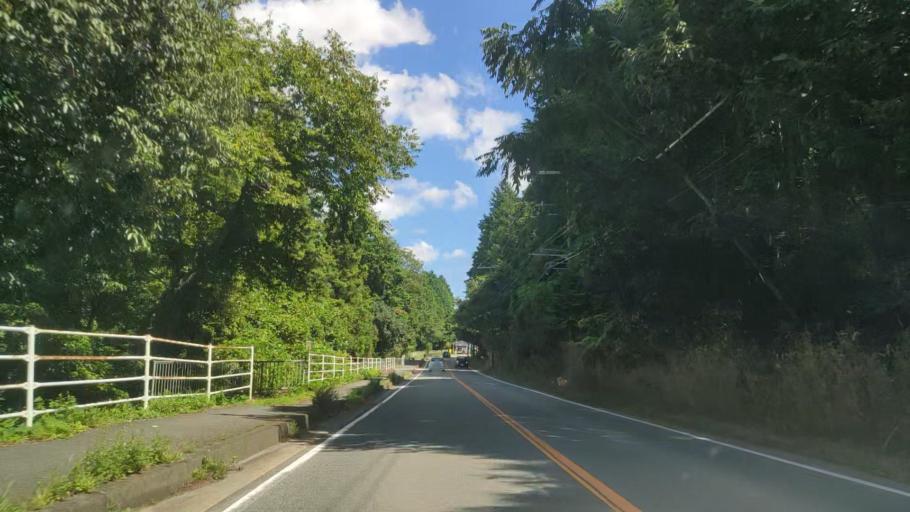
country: JP
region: Hyogo
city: Nishiwaki
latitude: 35.1306
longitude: 135.0119
